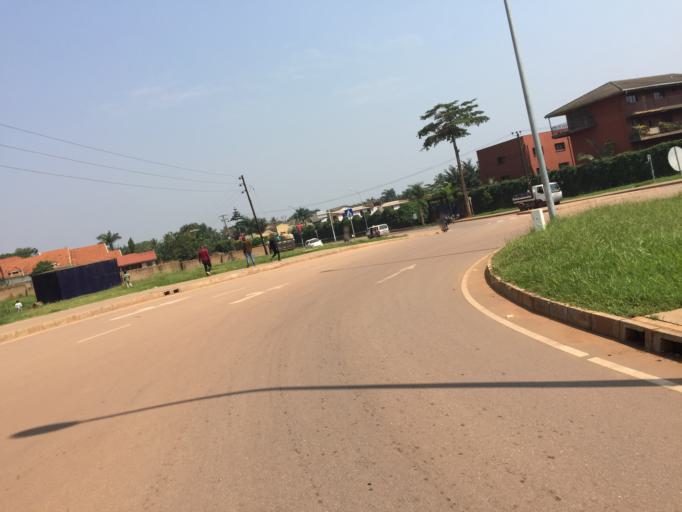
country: UG
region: Central Region
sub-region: Kampala District
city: Kampala
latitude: 0.2395
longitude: 32.6207
